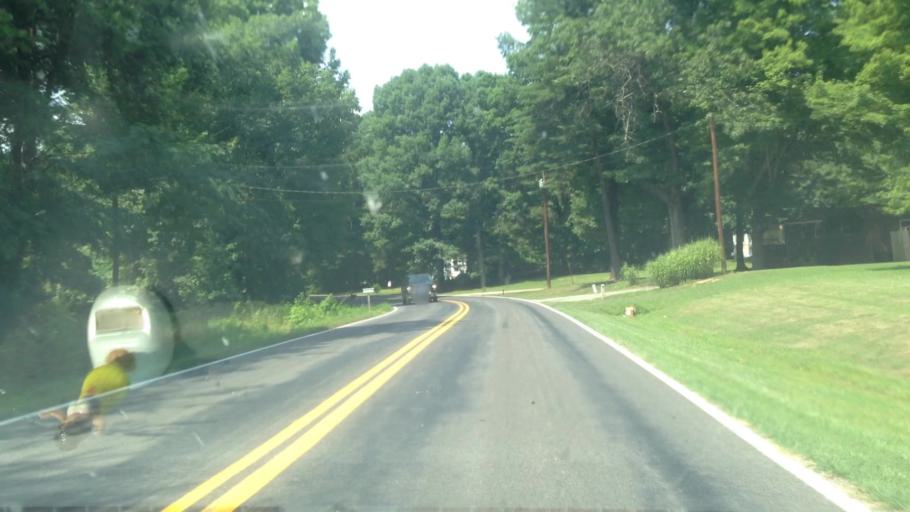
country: US
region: North Carolina
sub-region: Stokes County
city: Walnut Cove
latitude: 36.2563
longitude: -80.0975
